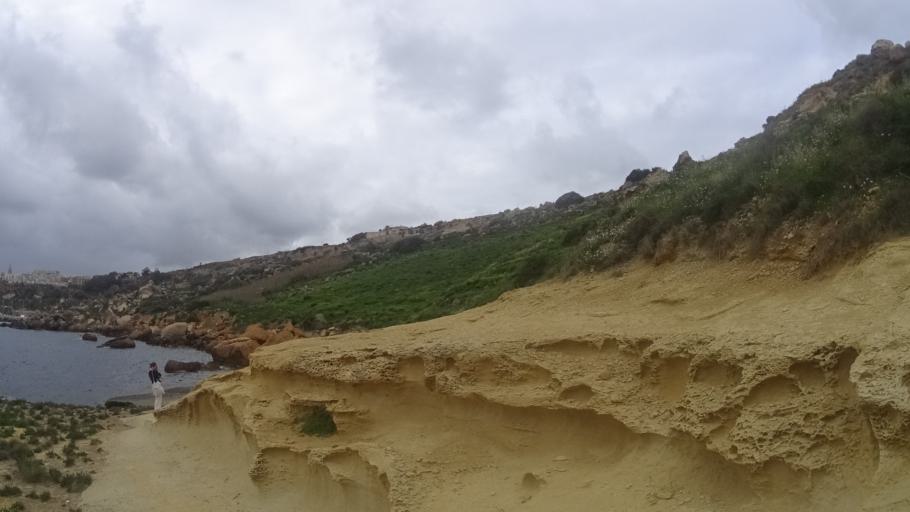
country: MT
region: Il-Qala
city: Qala
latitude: 36.0270
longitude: 14.3057
